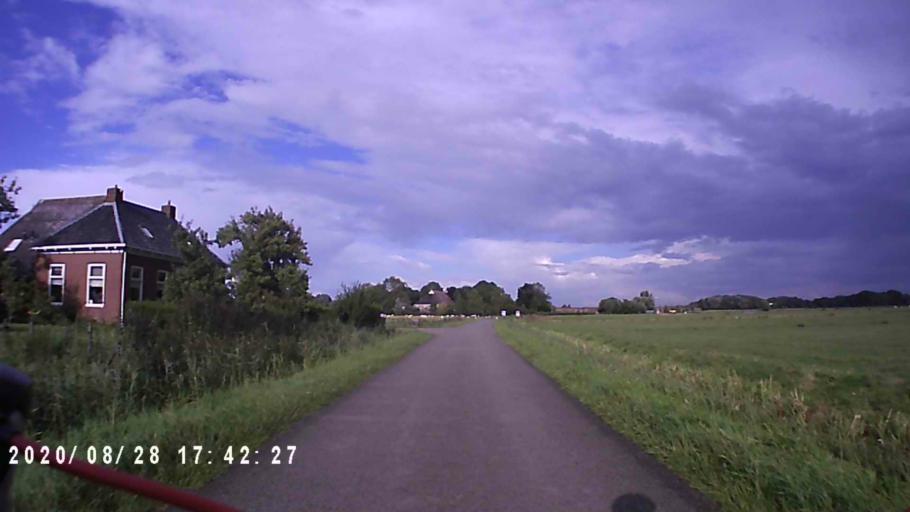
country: NL
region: Groningen
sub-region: Gemeente Zuidhorn
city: Aduard
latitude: 53.2481
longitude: 6.5077
